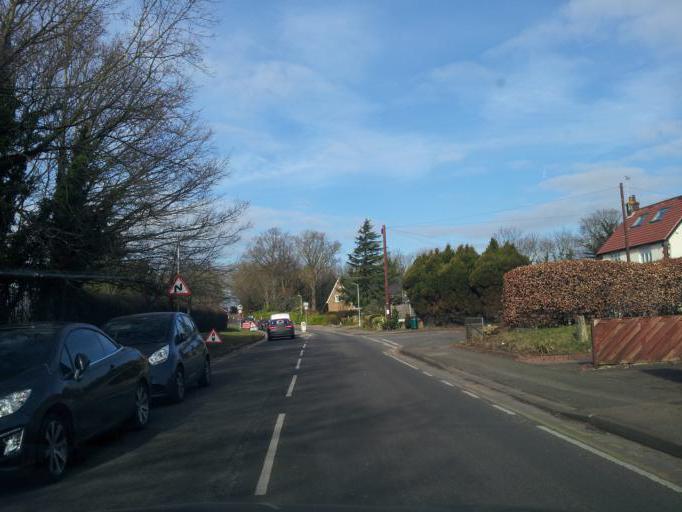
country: GB
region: England
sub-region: Hertfordshire
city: St Albans
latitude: 51.7485
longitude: -0.2887
